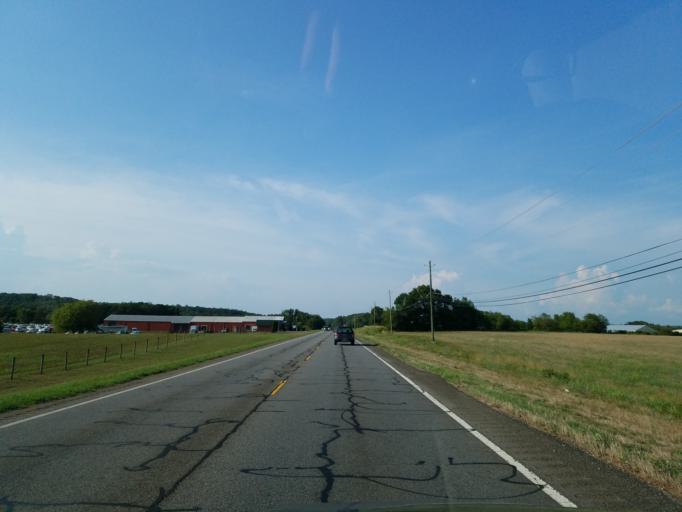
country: US
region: Georgia
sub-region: Bartow County
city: Rydal
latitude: 34.3242
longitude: -84.7184
